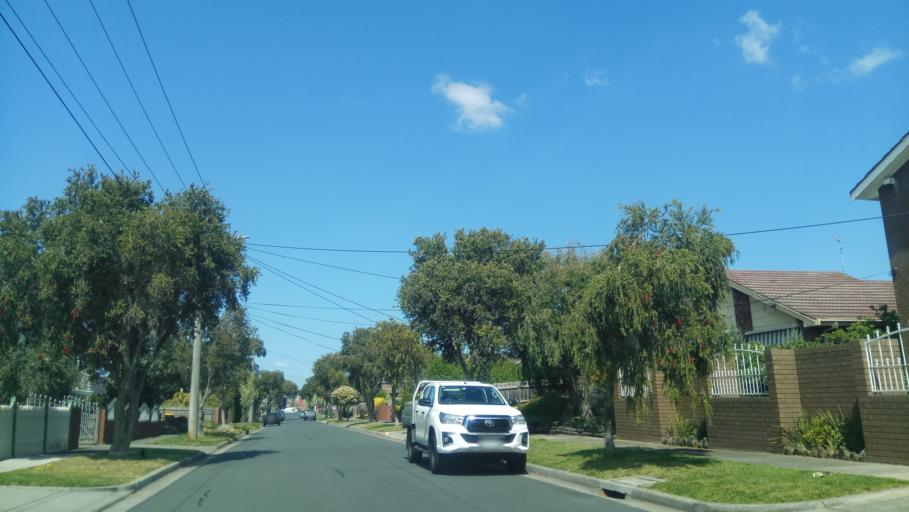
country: AU
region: Victoria
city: Heatherton
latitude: -37.9667
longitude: 145.0850
